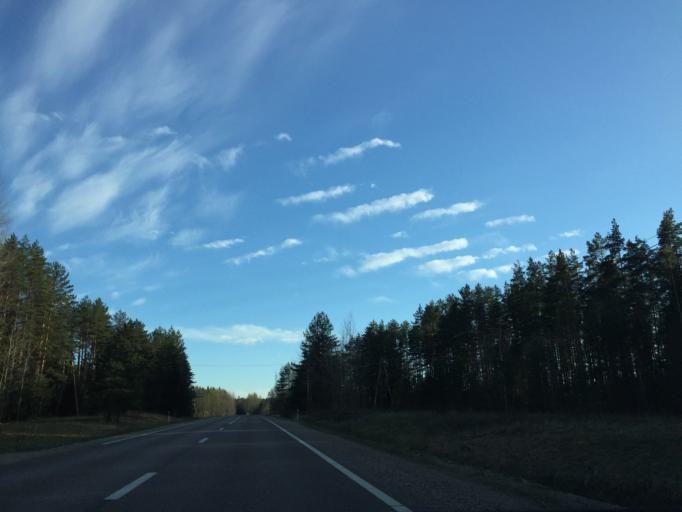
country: LV
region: Valkas Rajons
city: Valka
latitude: 57.7306
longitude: 25.9401
